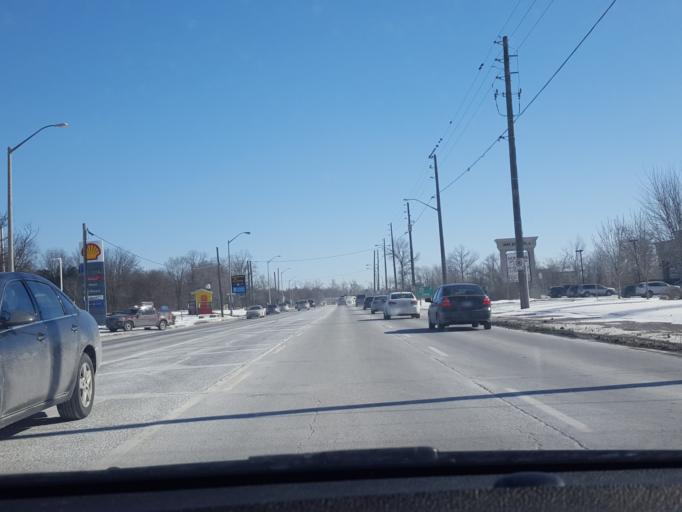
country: CA
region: Ontario
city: Cambridge
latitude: 43.4043
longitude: -80.3860
